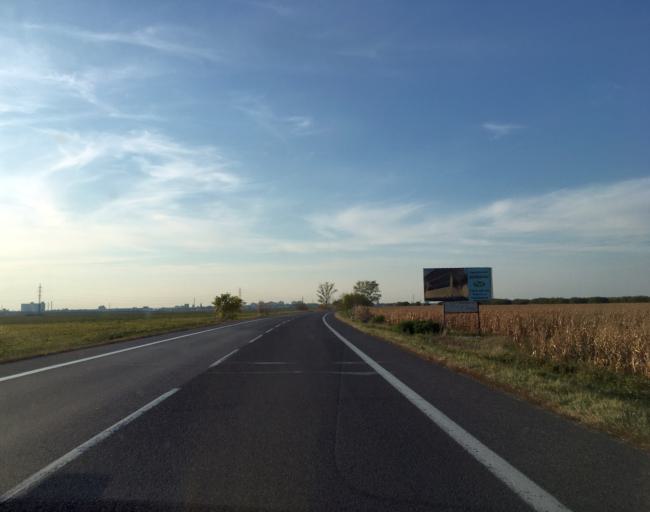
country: SK
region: Trnavsky
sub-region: Okres Galanta
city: Galanta
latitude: 48.1828
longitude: 17.7698
